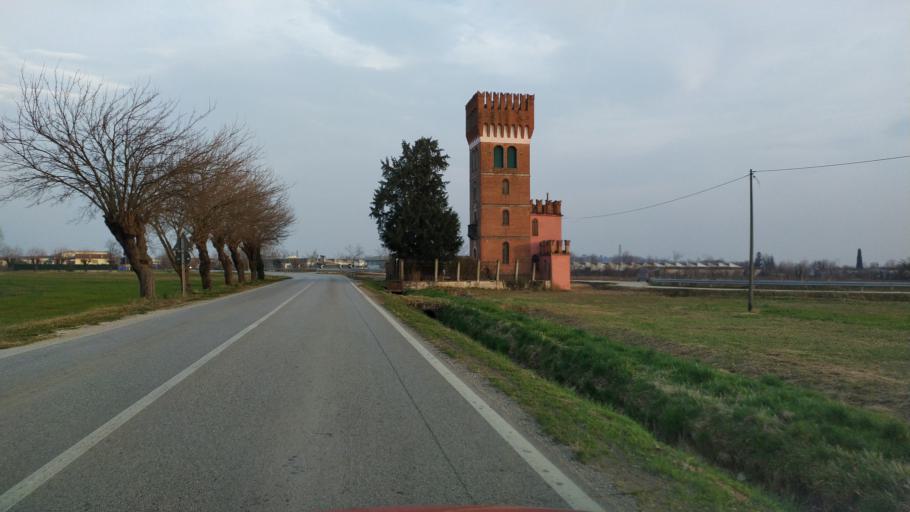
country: IT
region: Veneto
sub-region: Provincia di Vicenza
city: Sarcedo
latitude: 45.6866
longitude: 11.5251
